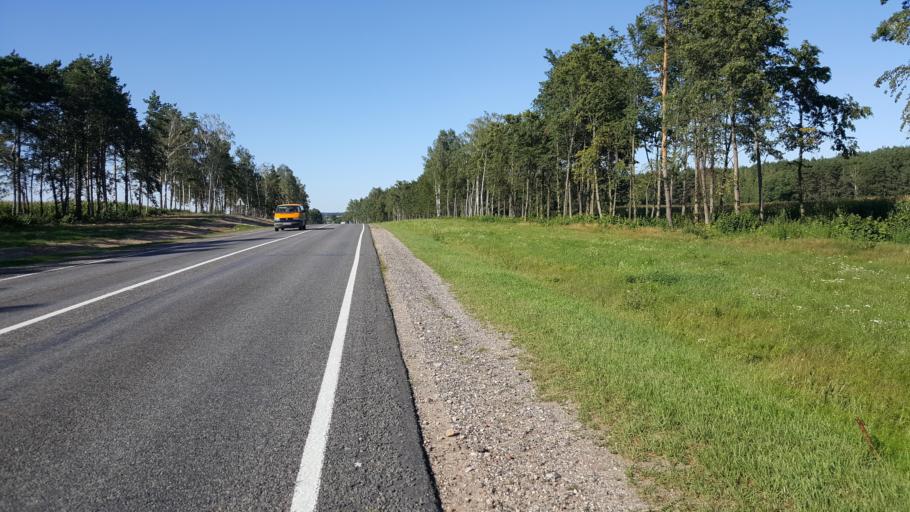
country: BY
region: Brest
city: Charnawchytsy
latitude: 52.2911
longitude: 23.7758
